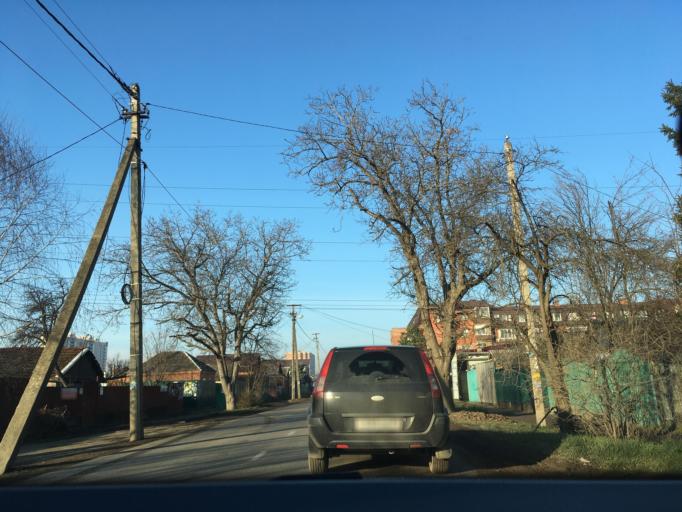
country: RU
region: Krasnodarskiy
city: Krasnodar
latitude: 45.0784
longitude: 39.0207
